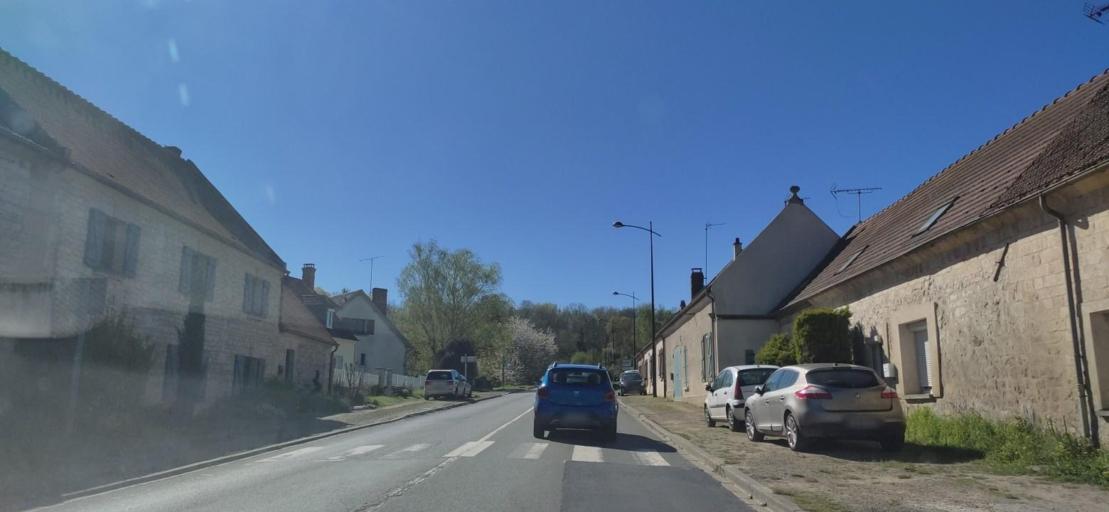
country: FR
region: Picardie
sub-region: Departement de l'Oise
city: Villers-sur-Coudun
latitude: 49.4636
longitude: 2.7611
